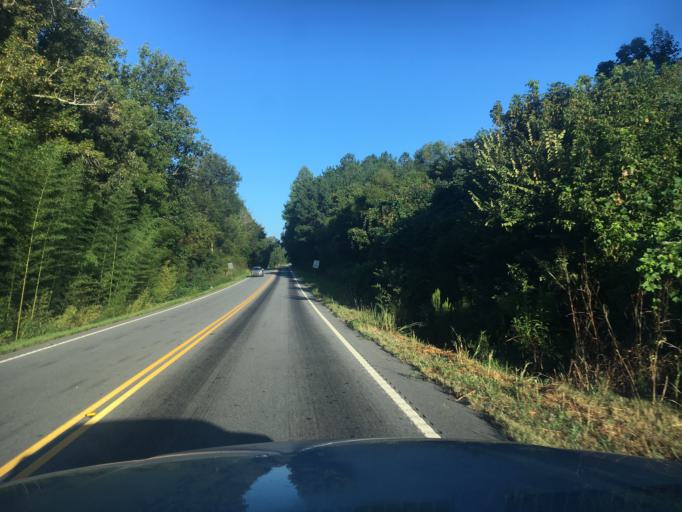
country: US
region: South Carolina
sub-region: Spartanburg County
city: Woodruff
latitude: 34.6991
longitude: -81.9441
